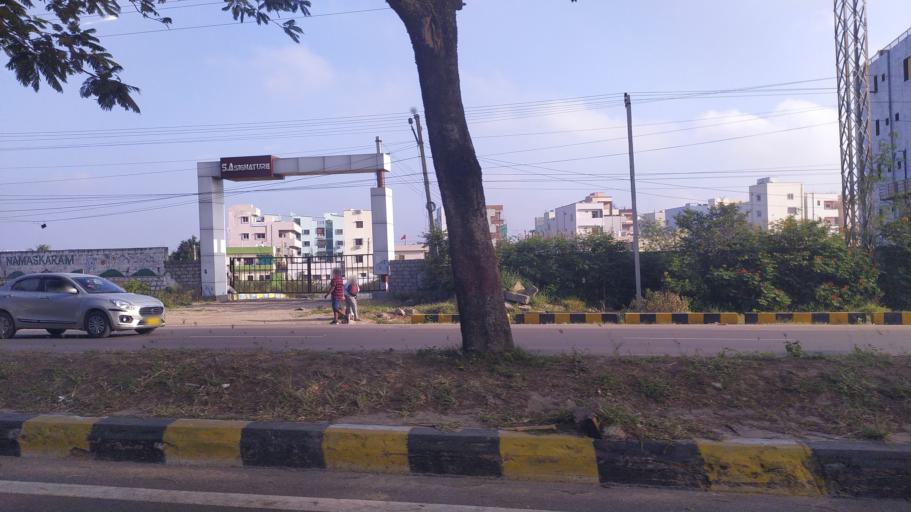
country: IN
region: Telangana
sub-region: Rangareddi
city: Balapur
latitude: 17.3158
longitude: 78.4415
